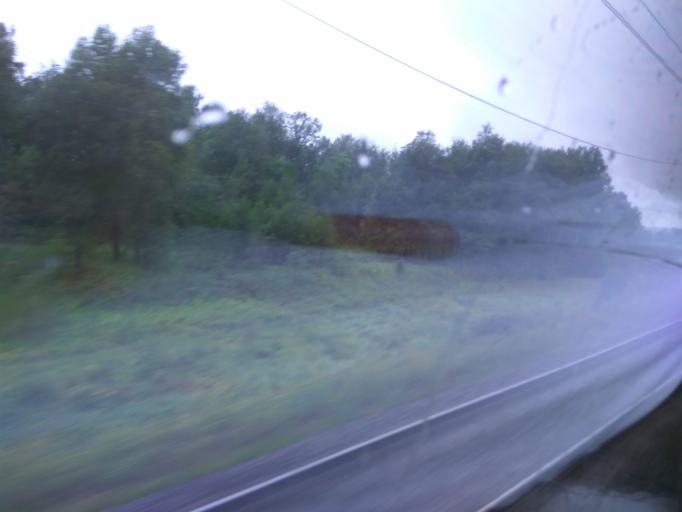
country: RU
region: Moskovskaya
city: Kashira
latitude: 54.8538
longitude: 38.2167
